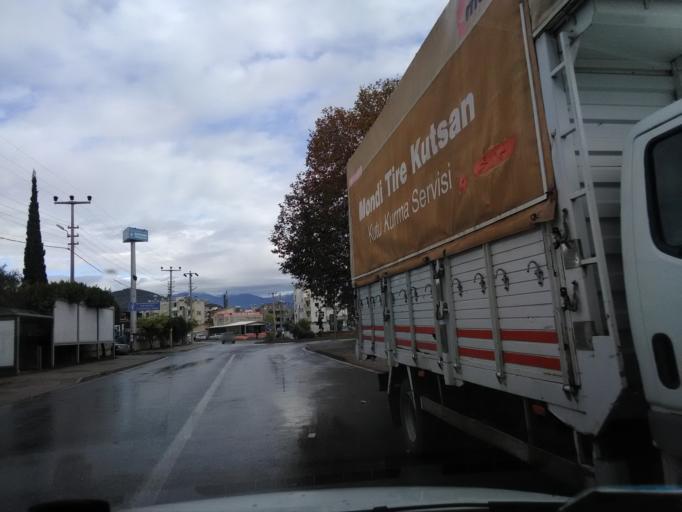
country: TR
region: Antalya
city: Gazipasa
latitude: 36.2772
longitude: 32.3162
